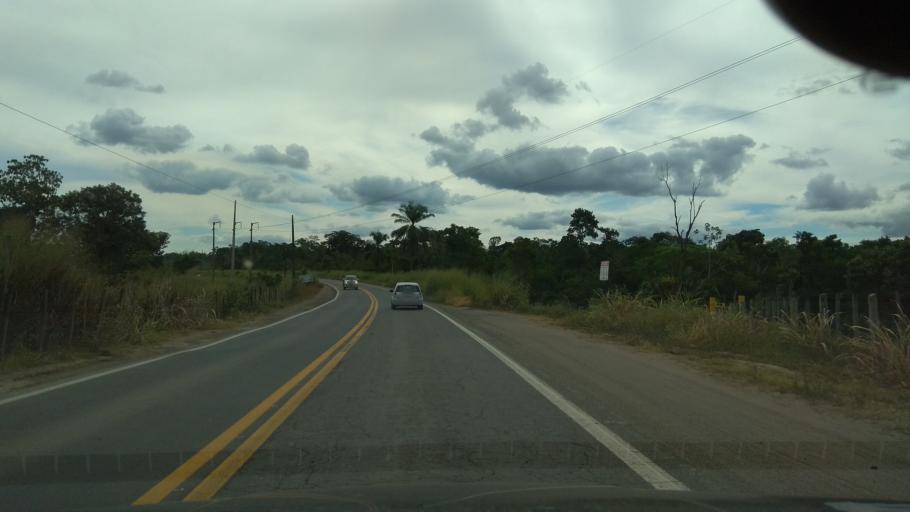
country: BR
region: Bahia
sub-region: Ipiau
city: Ipiau
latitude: -14.1492
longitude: -39.7007
